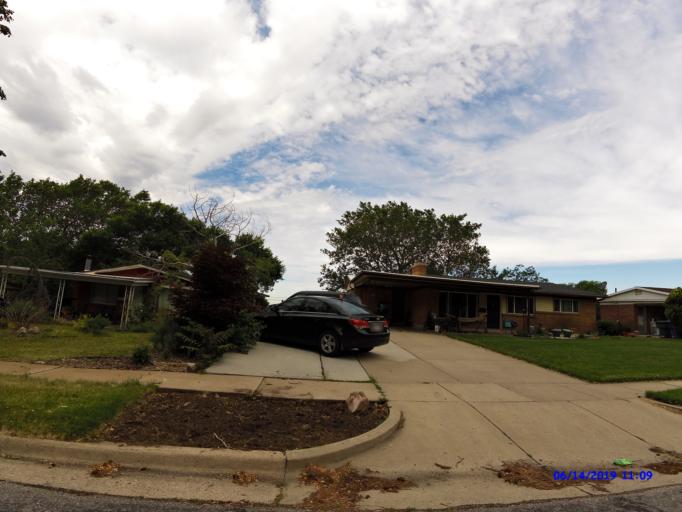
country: US
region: Utah
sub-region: Weber County
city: Ogden
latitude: 41.2477
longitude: -111.9368
